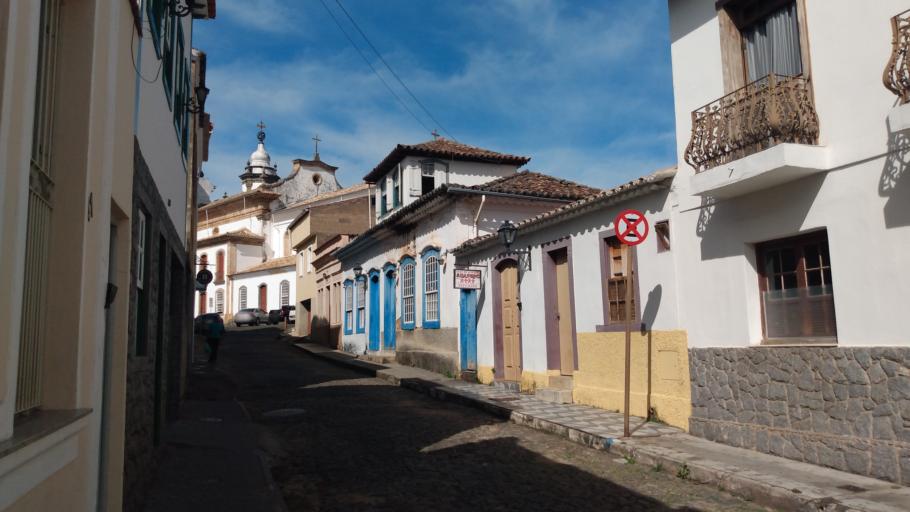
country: BR
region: Minas Gerais
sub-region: Sao Joao Del Rei
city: Sao Joao del Rei
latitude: -21.1331
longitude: -44.2602
